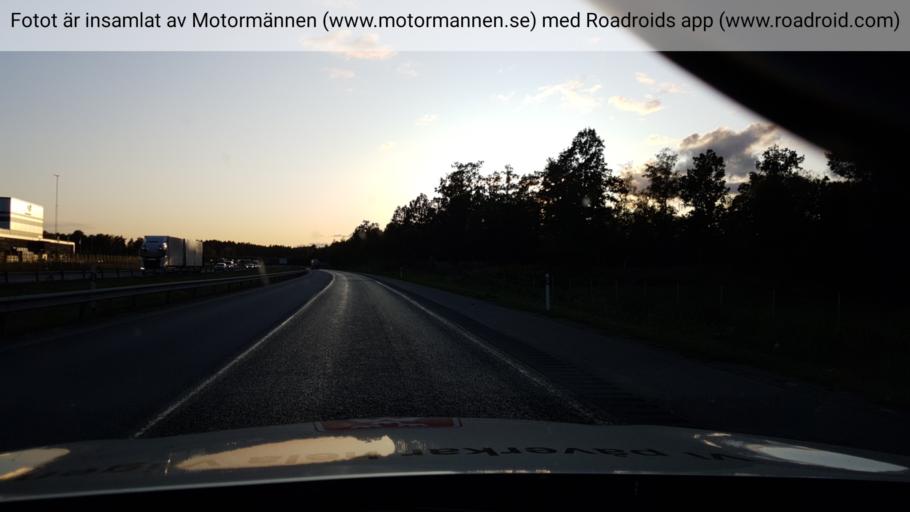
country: SE
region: OErebro
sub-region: Orebro Kommun
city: Hovsta
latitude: 59.3076
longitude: 15.2693
